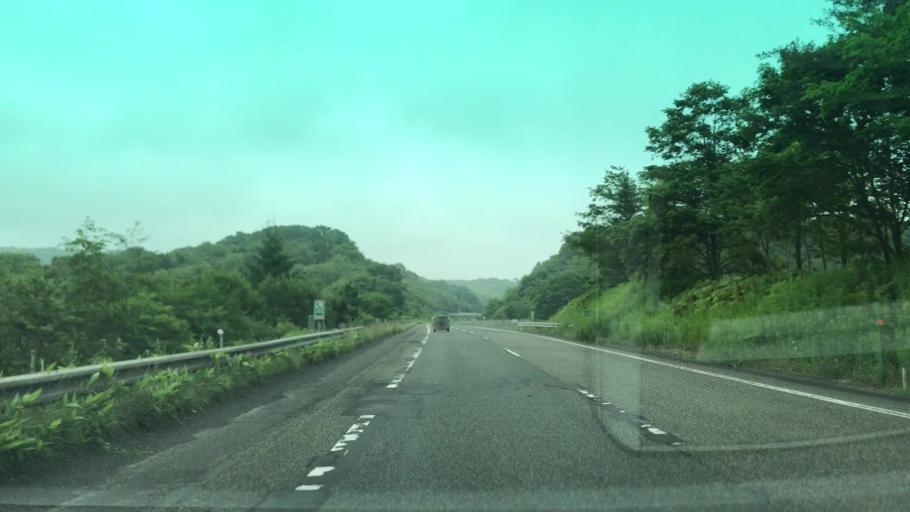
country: JP
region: Hokkaido
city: Shiraoi
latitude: 42.4771
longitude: 141.2184
